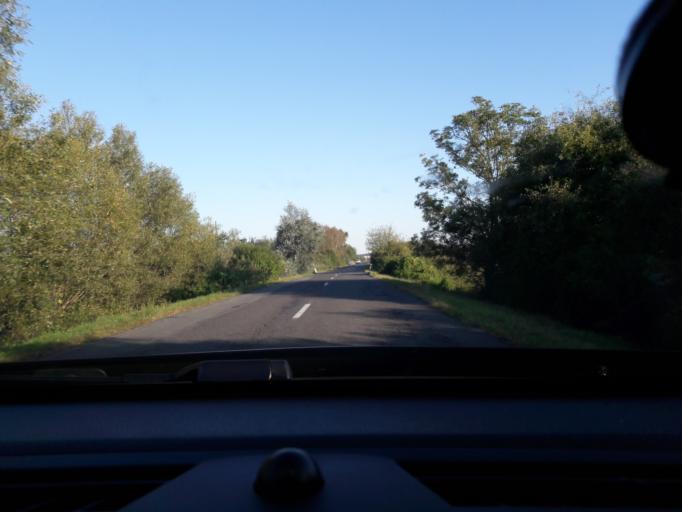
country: SK
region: Kosicky
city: Michalovce
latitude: 48.6200
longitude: 21.9399
